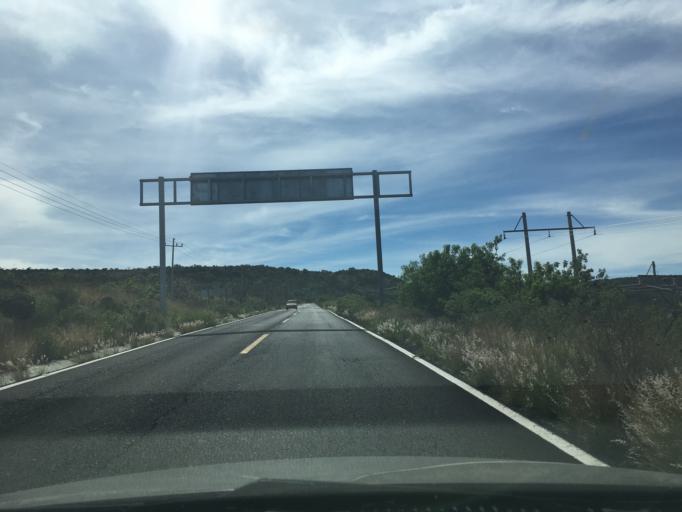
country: MX
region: Guanajuato
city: Coroneo
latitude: 20.1903
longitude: -100.3465
